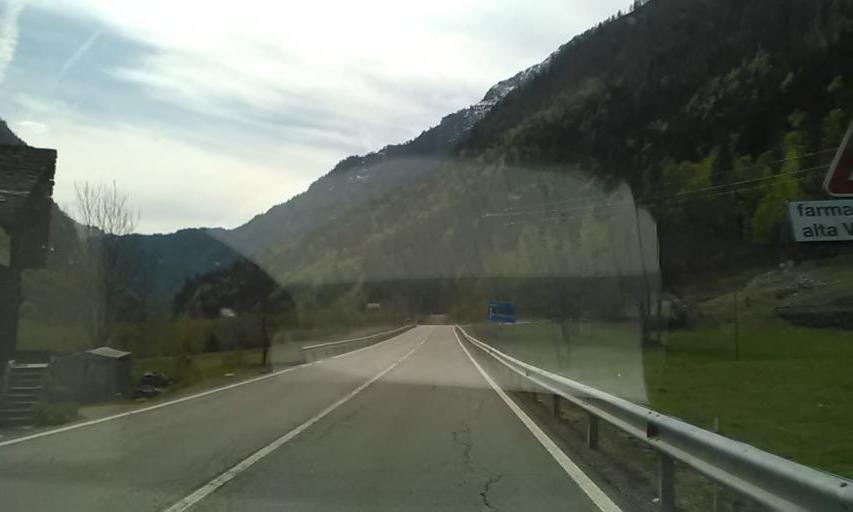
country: IT
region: Piedmont
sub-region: Provincia di Vercelli
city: Riva Valdobbia
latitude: 45.8279
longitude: 7.9637
